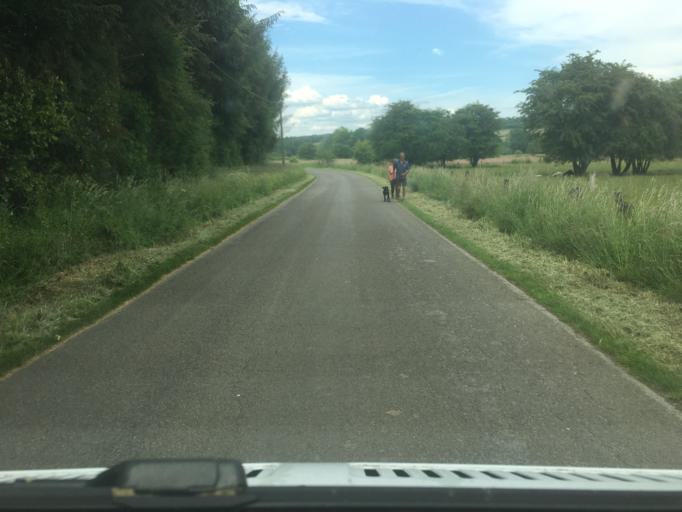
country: BE
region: Wallonia
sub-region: Province du Luxembourg
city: Florenville
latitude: 49.7142
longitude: 5.2598
